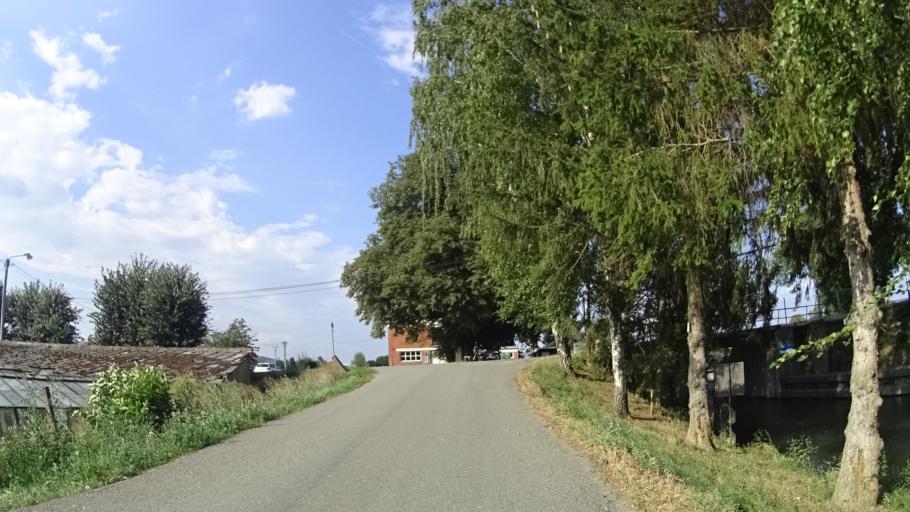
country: CZ
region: Zlin
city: Spytihnev
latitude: 49.1352
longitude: 17.5012
